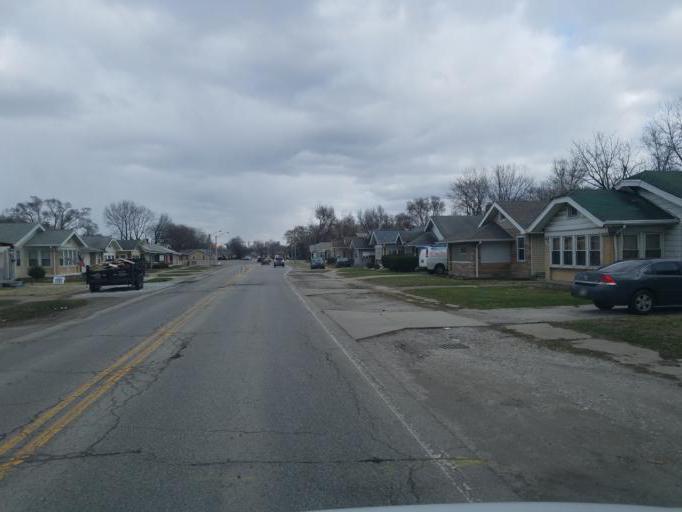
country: US
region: Indiana
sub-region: Marion County
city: Speedway
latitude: 39.7627
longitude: -86.2272
